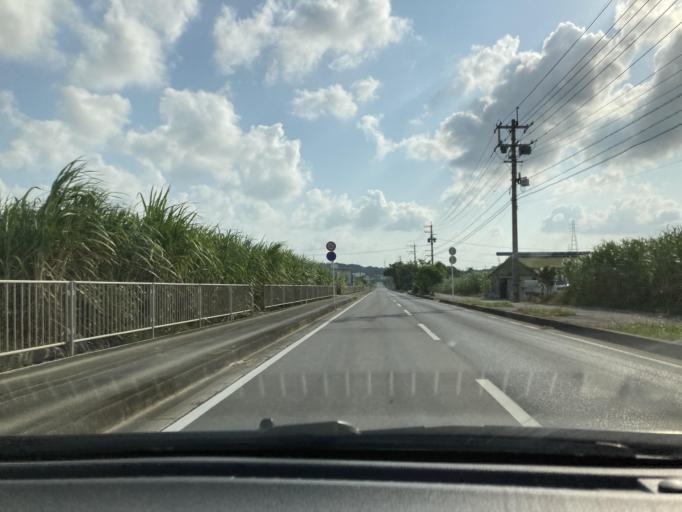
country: JP
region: Okinawa
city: Itoman
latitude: 26.1462
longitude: 127.7052
